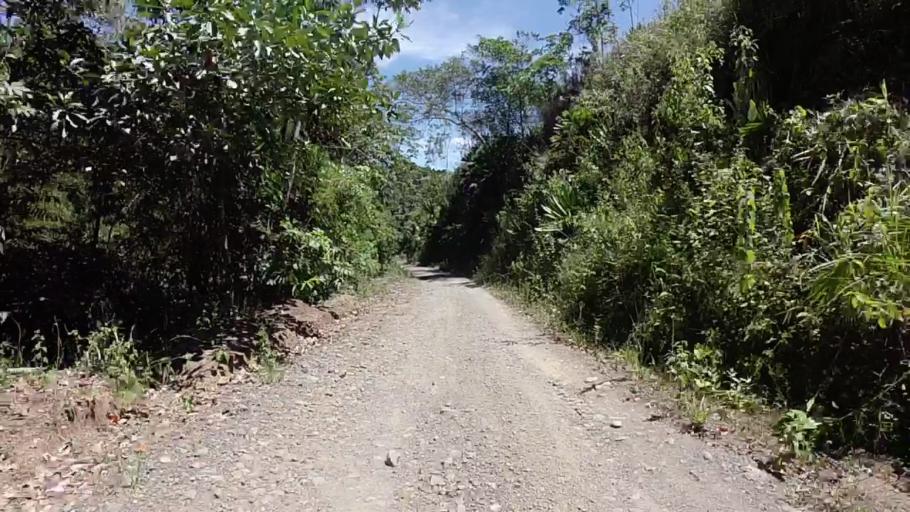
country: CO
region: Valle del Cauca
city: Alcala
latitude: 4.7035
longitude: -75.8253
